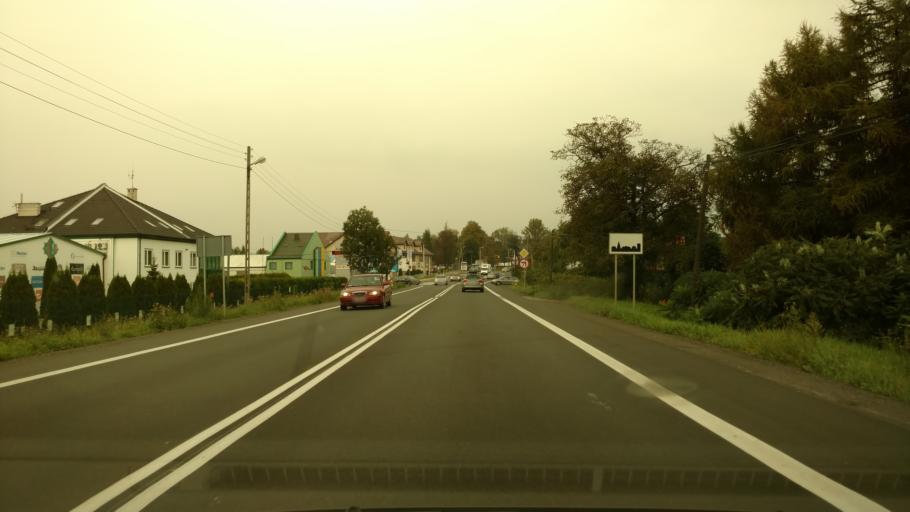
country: PL
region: Lesser Poland Voivodeship
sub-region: Powiat krakowski
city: Zielonki
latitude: 50.1121
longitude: 19.9661
